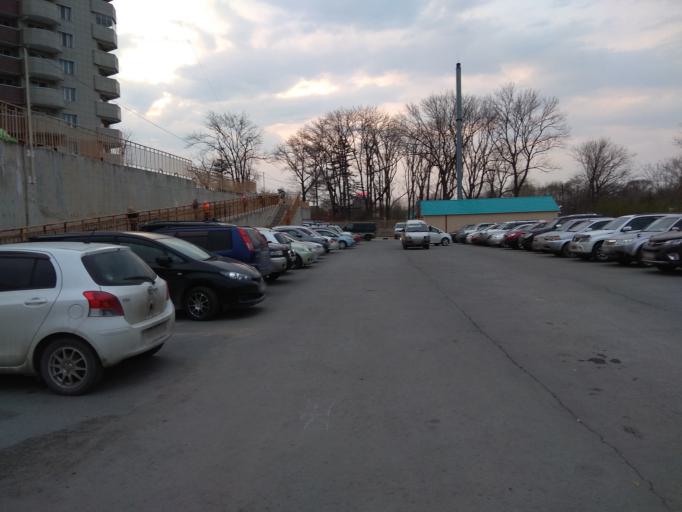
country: RU
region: Primorskiy
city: Trudovoye
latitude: 43.2237
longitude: 132.0040
